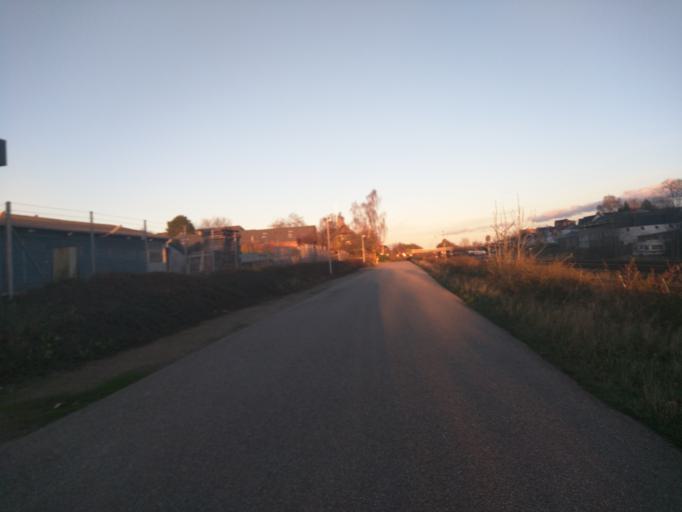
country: DK
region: Central Jutland
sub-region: Skanderborg Kommune
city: Horning
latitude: 56.0805
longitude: 10.0335
